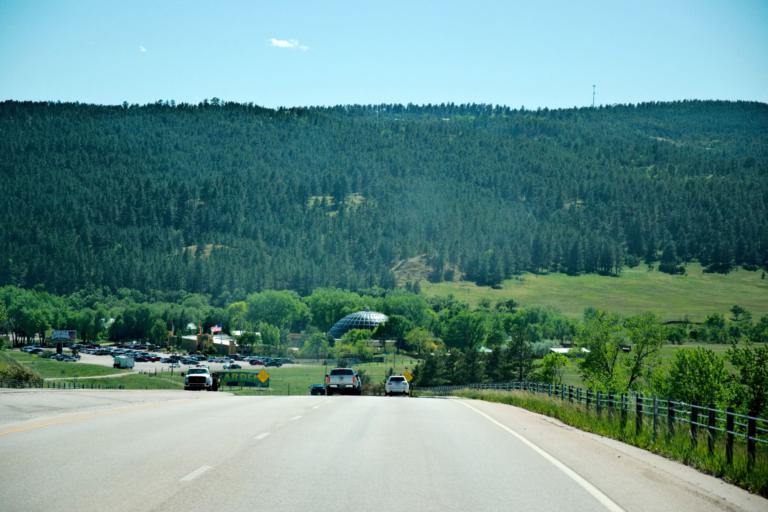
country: US
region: South Dakota
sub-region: Pennington County
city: Colonial Pine Hills
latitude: 43.9936
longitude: -103.2667
